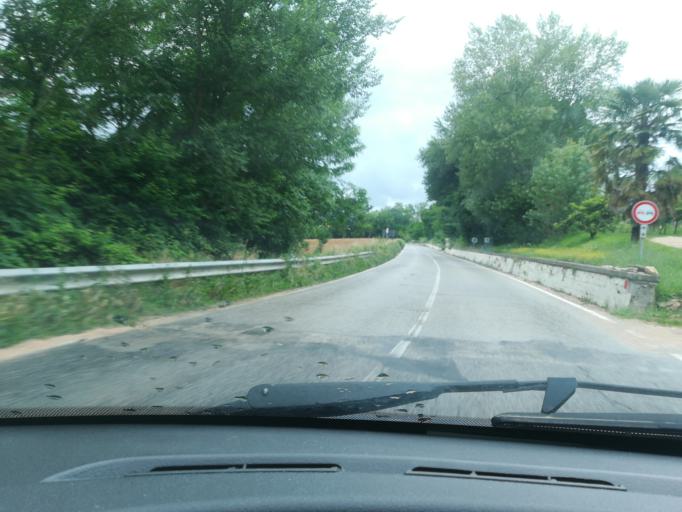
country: IT
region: The Marches
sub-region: Provincia di Macerata
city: San Ginesio
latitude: 43.1046
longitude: 13.3561
